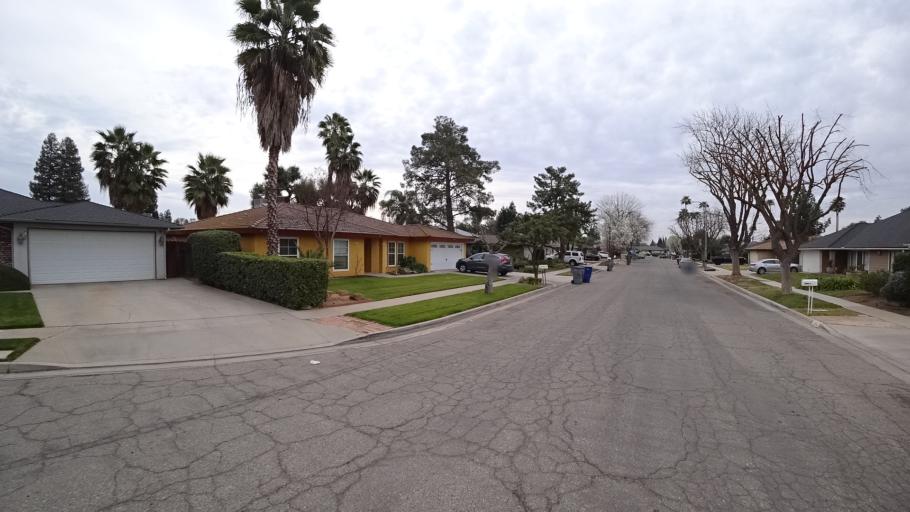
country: US
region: California
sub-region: Fresno County
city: Clovis
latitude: 36.8460
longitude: -119.7686
